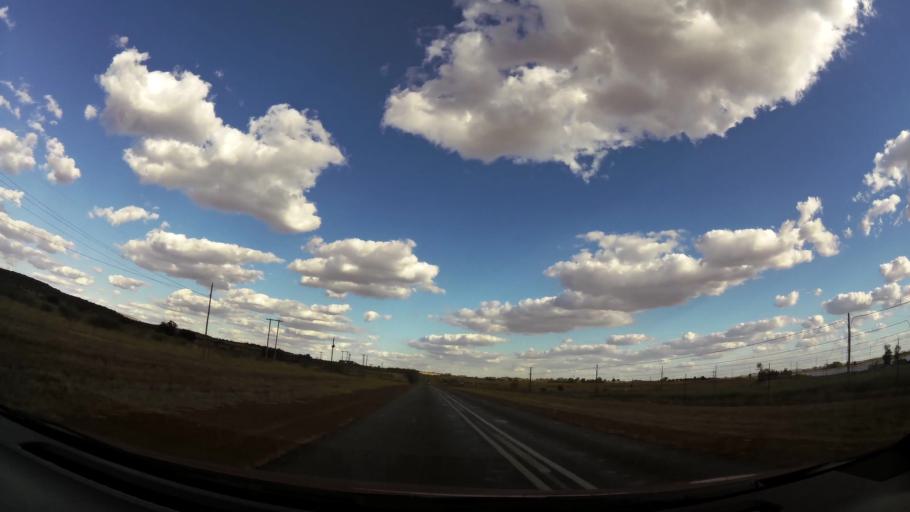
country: ZA
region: North-West
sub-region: Dr Kenneth Kaunda District Municipality
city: Potchefstroom
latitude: -26.5360
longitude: 27.1325
